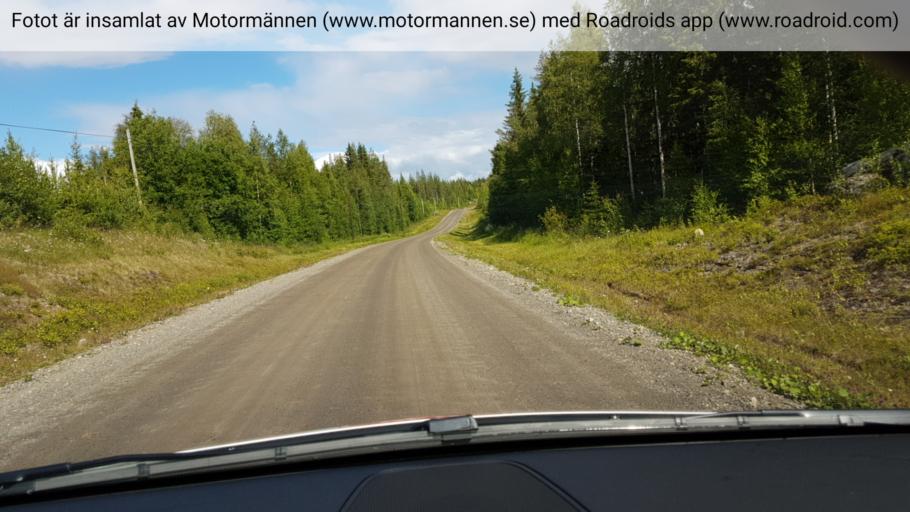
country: SE
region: Vaesterbotten
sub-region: Dorotea Kommun
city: Dorotea
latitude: 64.0945
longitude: 16.4796
